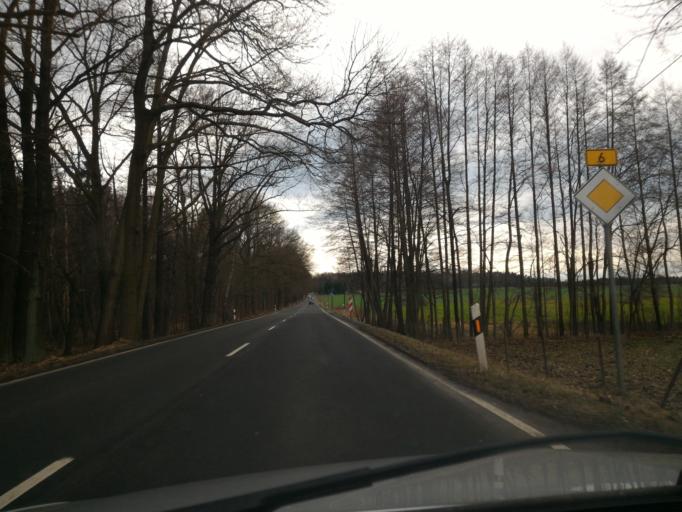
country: DE
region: Saxony
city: Arnsdorf
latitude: 51.0748
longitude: 14.0162
